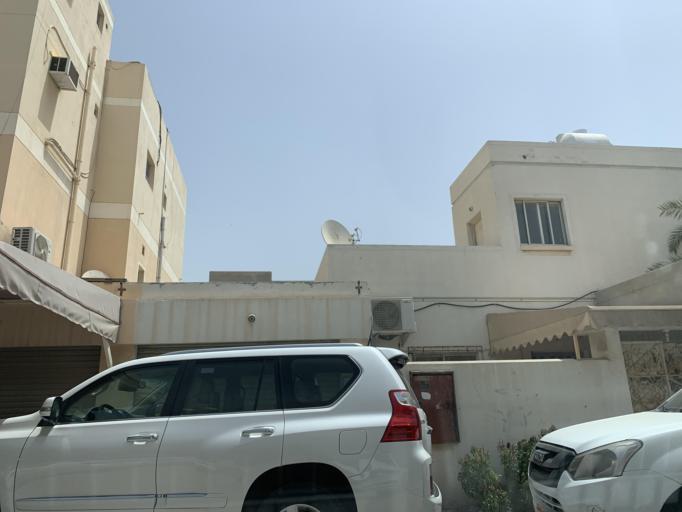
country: BH
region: Northern
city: Madinat `Isa
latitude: 26.1638
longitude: 50.5267
